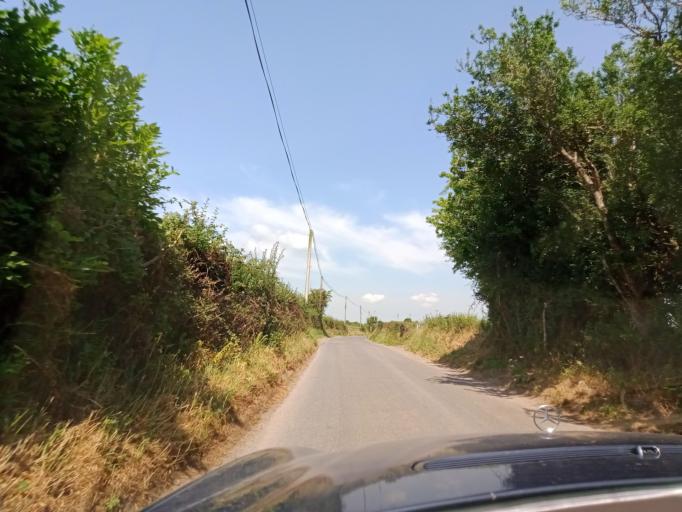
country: IE
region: Leinster
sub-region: Kilkenny
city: Mooncoin
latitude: 52.2864
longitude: -7.2350
